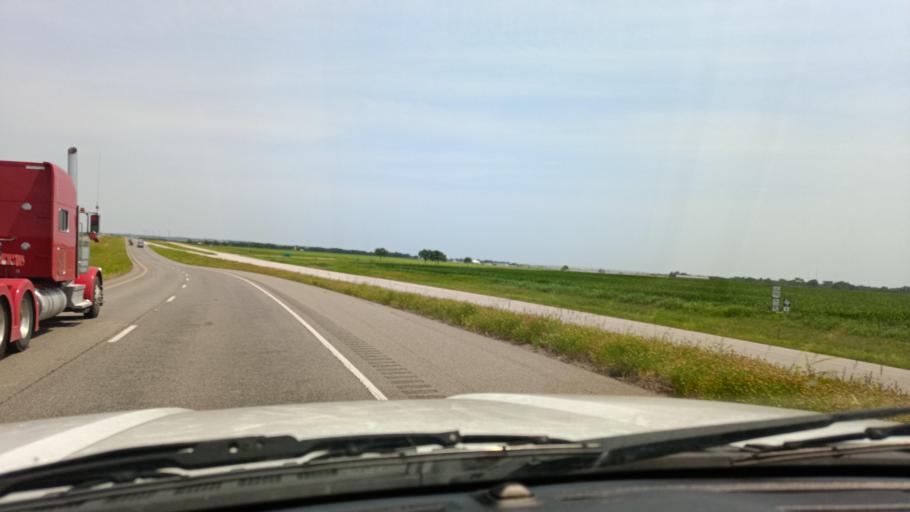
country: US
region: Texas
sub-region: Bell County
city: Little River-Academy
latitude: 31.0226
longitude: -97.3139
